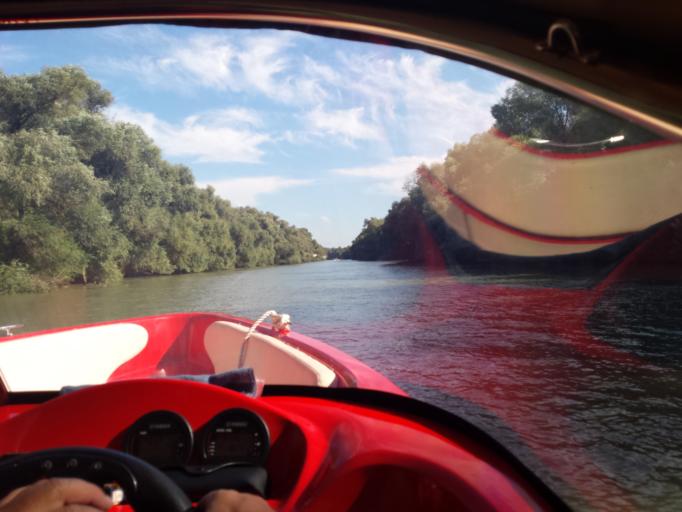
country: RO
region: Tulcea
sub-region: Comuna Pardina
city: Pardina
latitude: 45.2440
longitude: 28.9214
